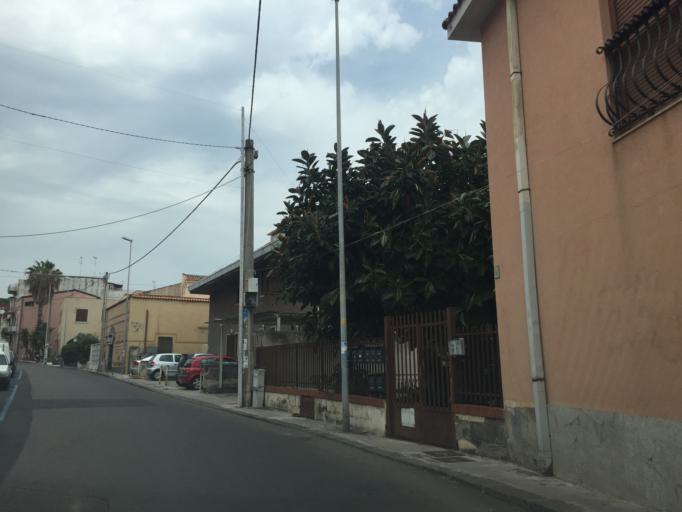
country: IT
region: Sicily
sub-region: Catania
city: Aci Trezza
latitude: 37.5671
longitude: 15.1641
